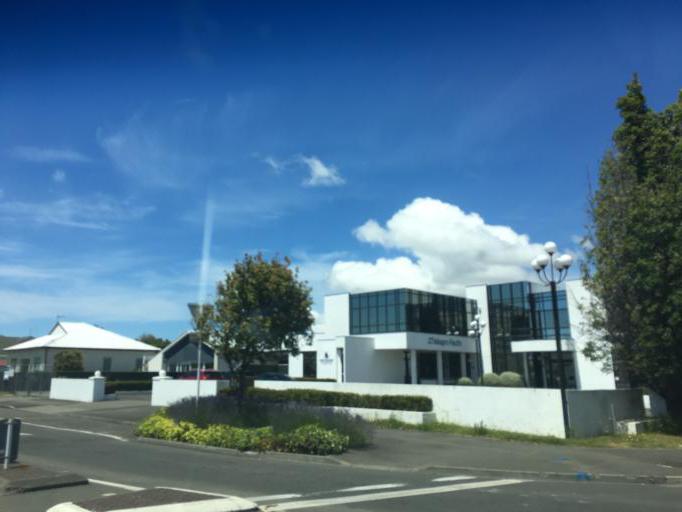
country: NZ
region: Hawke's Bay
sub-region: Hastings District
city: Hastings
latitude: -39.6341
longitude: 176.8350
